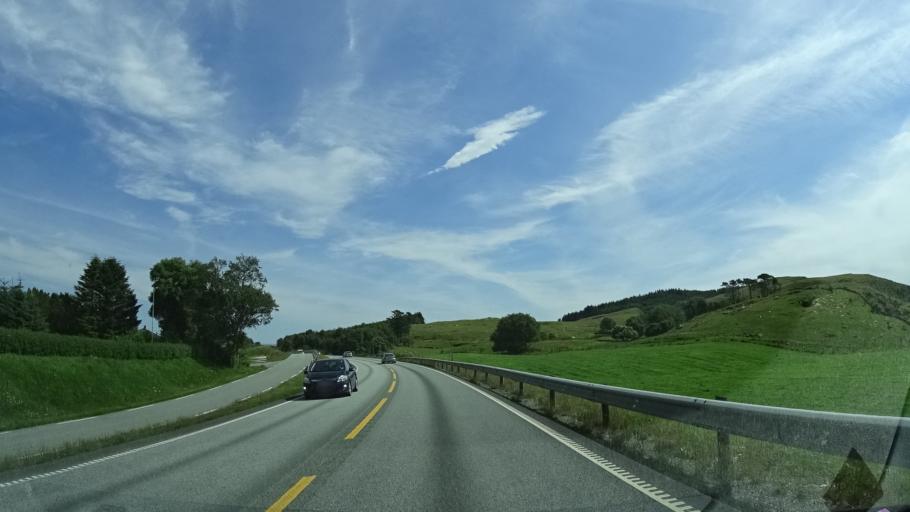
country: NO
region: Rogaland
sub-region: Rennesoy
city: Vikevag
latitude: 59.1259
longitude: 5.6504
